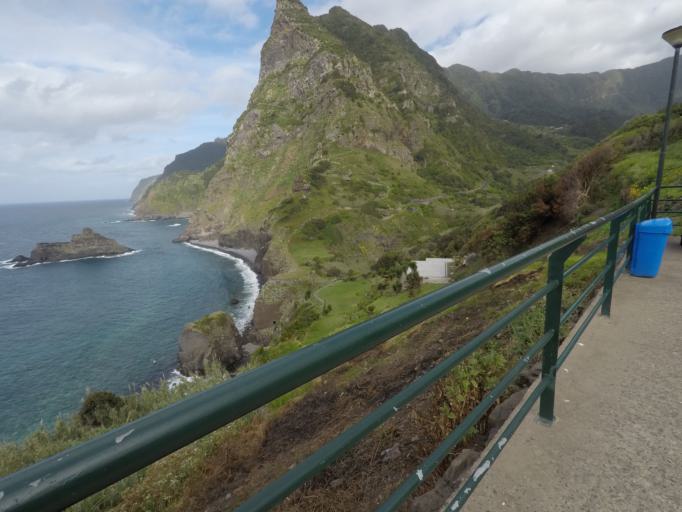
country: PT
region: Madeira
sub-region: Sao Vicente
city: Sao Vicente
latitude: 32.8270
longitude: -16.9729
